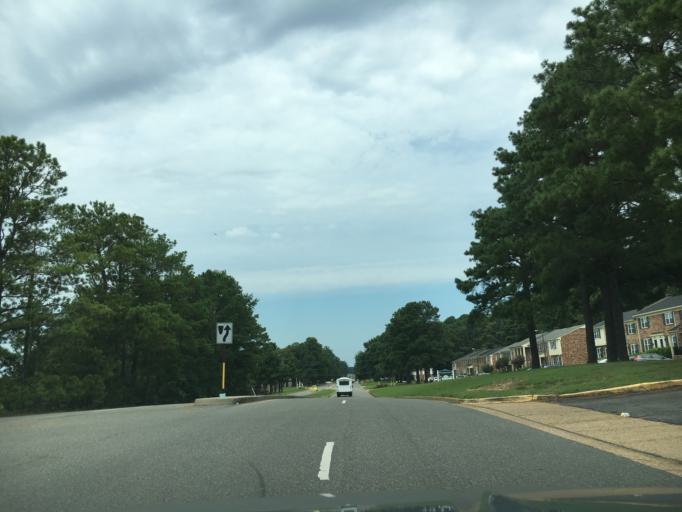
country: US
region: Virginia
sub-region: Henrico County
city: Short Pump
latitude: 37.5988
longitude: -77.6185
